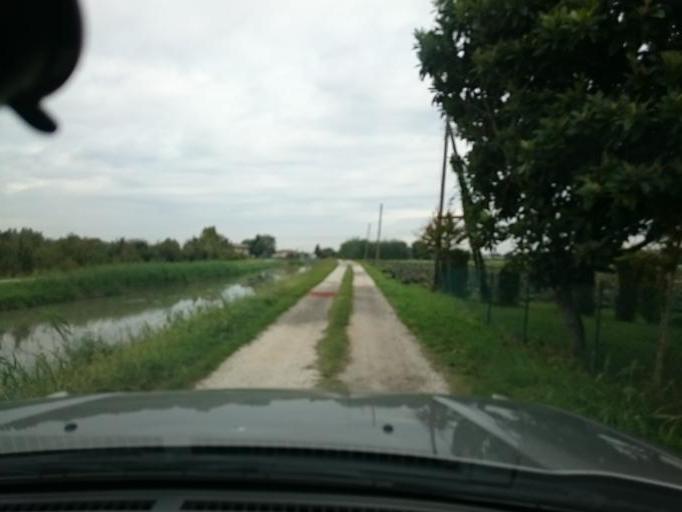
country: IT
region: Veneto
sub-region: Provincia di Padova
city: Codevigo
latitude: 45.2642
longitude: 12.0918
